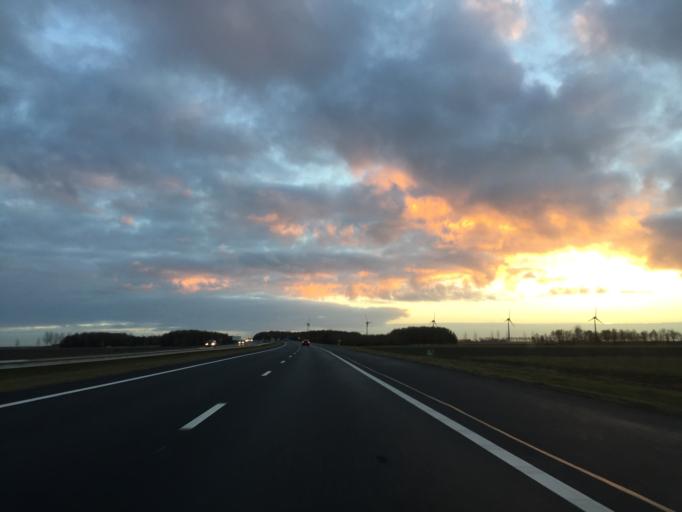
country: NL
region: Flevoland
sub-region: Gemeente Urk
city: Urk
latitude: 52.6516
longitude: 5.6795
